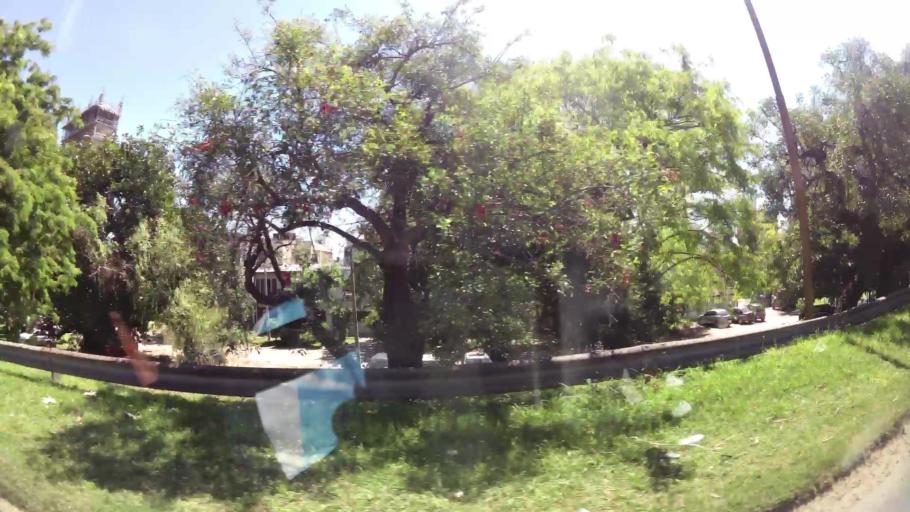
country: AR
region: Santa Fe
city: Santa Fe de la Vera Cruz
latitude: -31.6544
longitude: -60.7055
